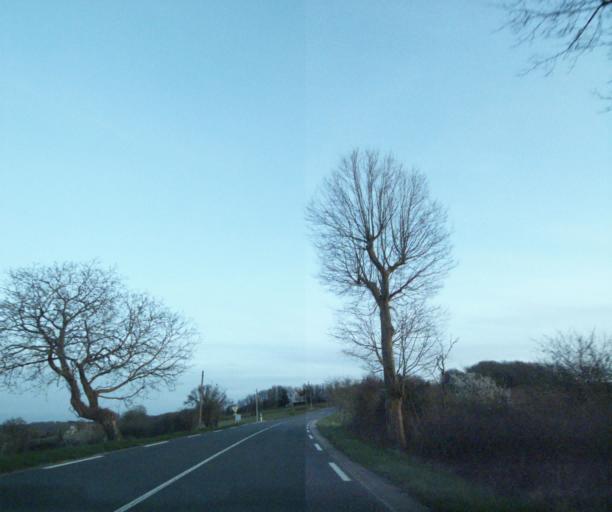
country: FR
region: Midi-Pyrenees
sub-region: Departement du Lot
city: Pradines
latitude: 44.5580
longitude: 1.4759
